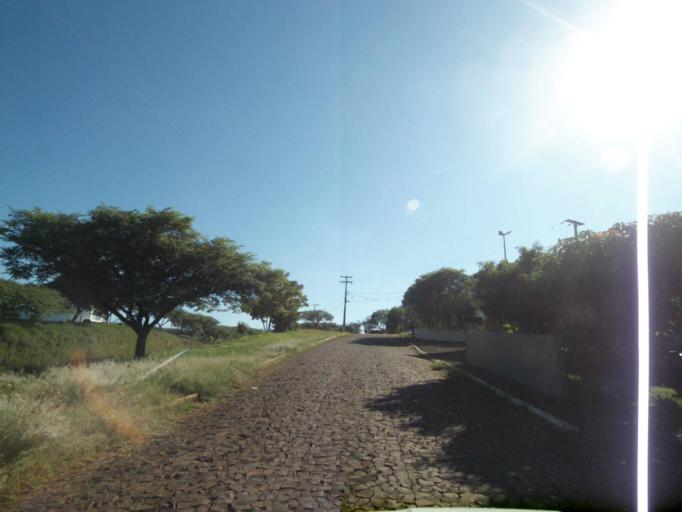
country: BR
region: Parana
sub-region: Laranjeiras Do Sul
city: Laranjeiras do Sul
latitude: -25.4875
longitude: -52.5247
